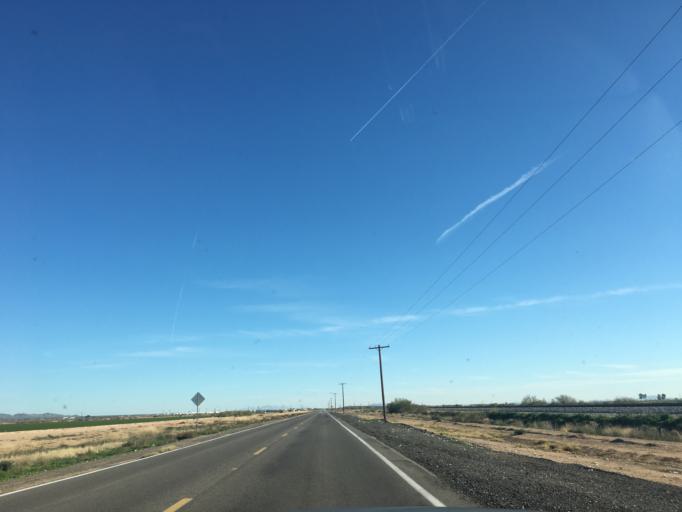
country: US
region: Arizona
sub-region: Pinal County
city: Maricopa
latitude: 33.0093
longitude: -111.9710
